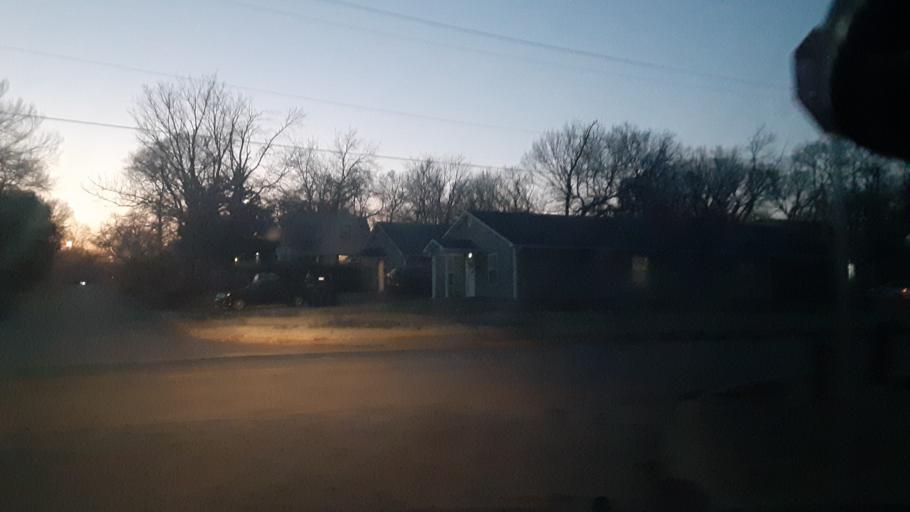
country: US
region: Oklahoma
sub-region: Payne County
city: Stillwater
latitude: 36.1113
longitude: -97.0693
